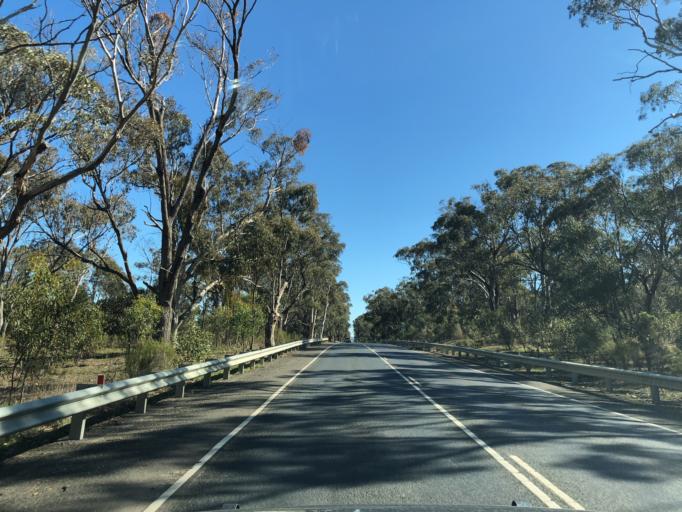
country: AU
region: Victoria
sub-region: Melton
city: Melton West
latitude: -37.6148
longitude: 144.5455
